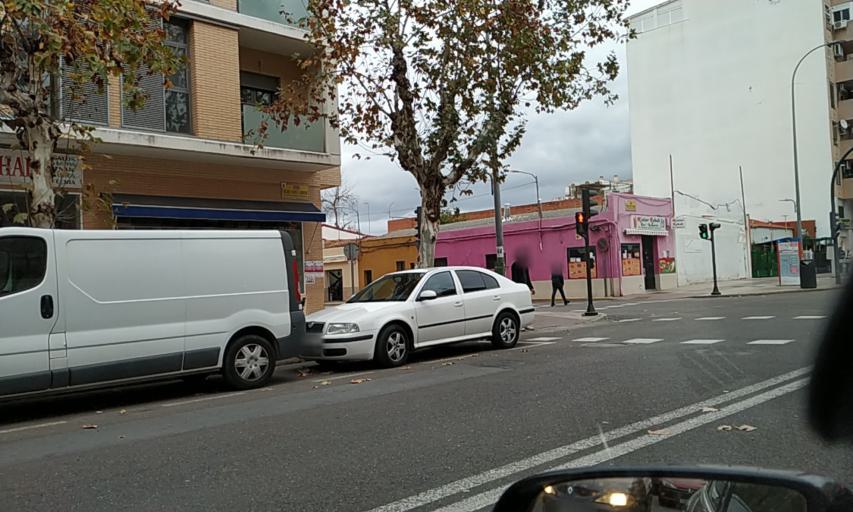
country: ES
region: Extremadura
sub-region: Provincia de Badajoz
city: Badajoz
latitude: 38.8790
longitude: -6.9560
